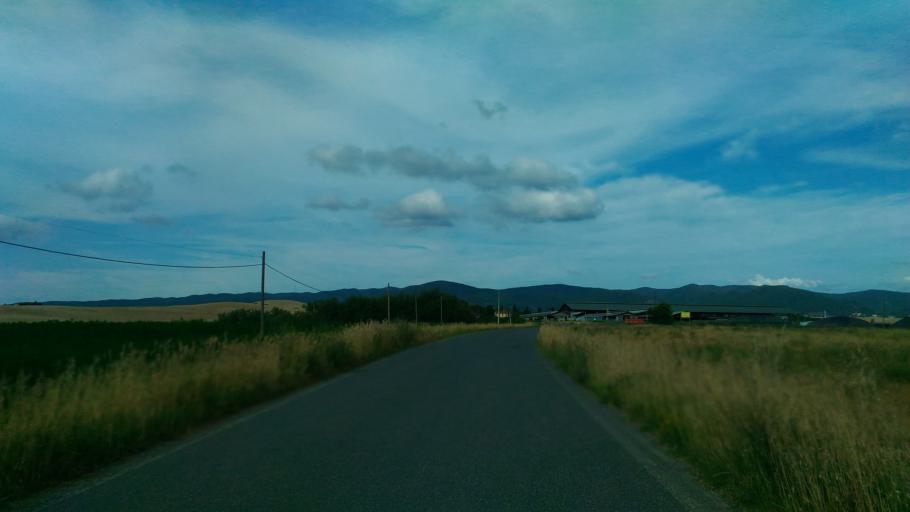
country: IT
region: Tuscany
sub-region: Provincia di Livorno
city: Rosignano Marittimo
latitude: 43.4417
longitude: 10.5008
